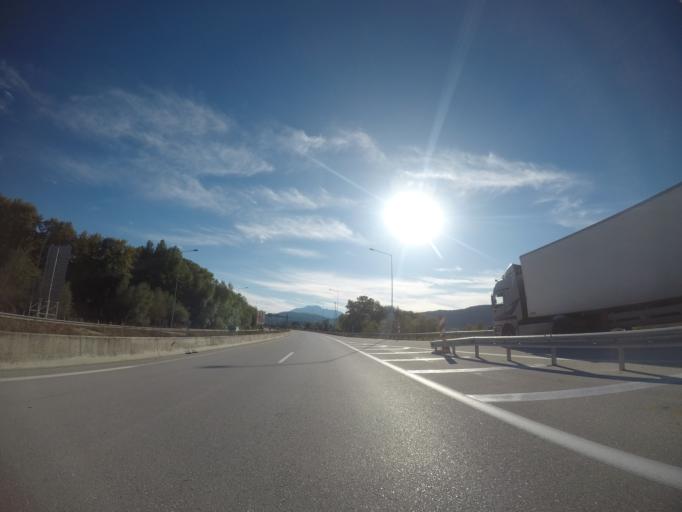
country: GR
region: Epirus
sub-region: Nomos Ioanninon
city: Koutselio
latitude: 39.6177
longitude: 20.9461
